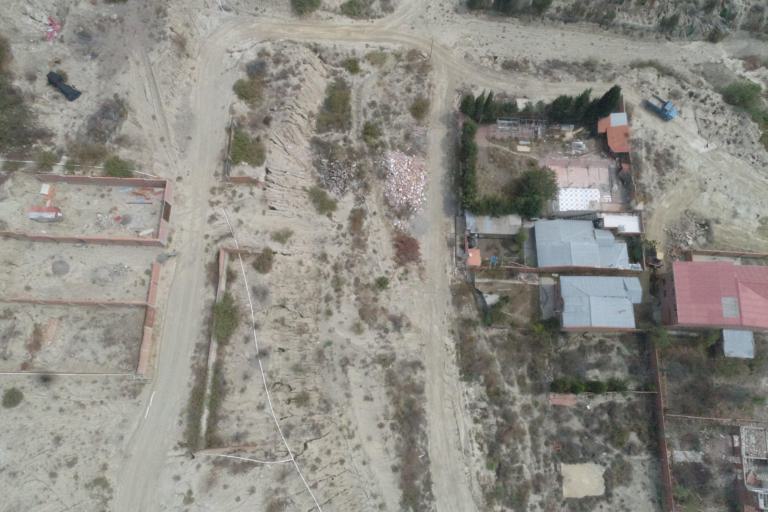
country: BO
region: La Paz
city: La Paz
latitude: -16.5990
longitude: -68.0684
